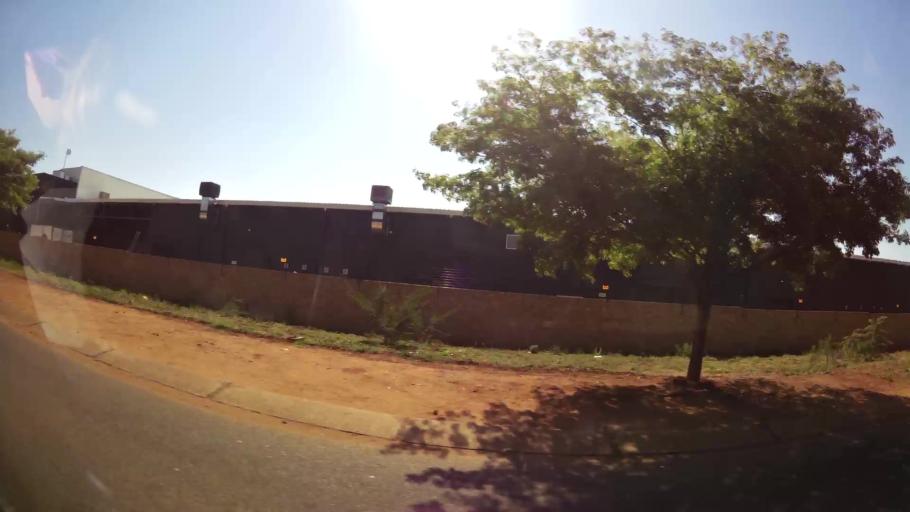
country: ZA
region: Gauteng
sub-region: City of Tshwane Metropolitan Municipality
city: Pretoria
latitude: -25.6850
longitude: 28.2759
